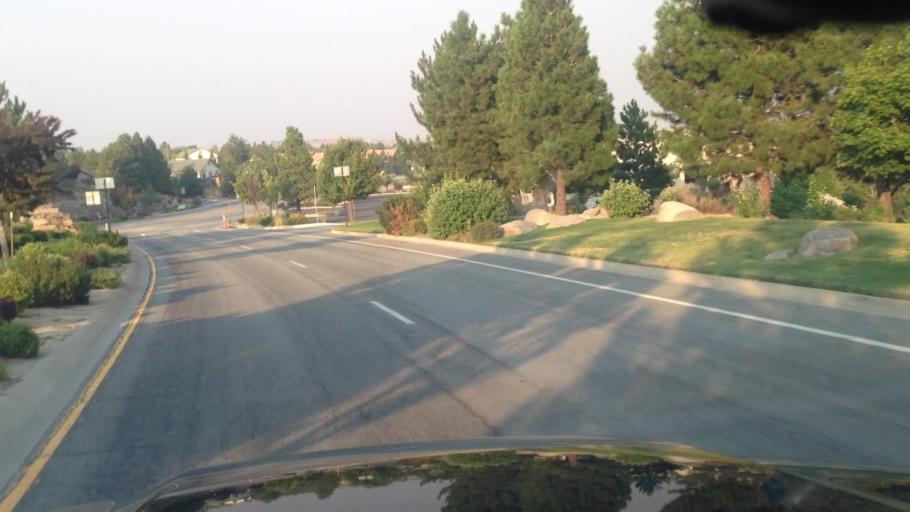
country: US
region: Nevada
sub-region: Washoe County
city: Mogul
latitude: 39.5189
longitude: -119.9037
